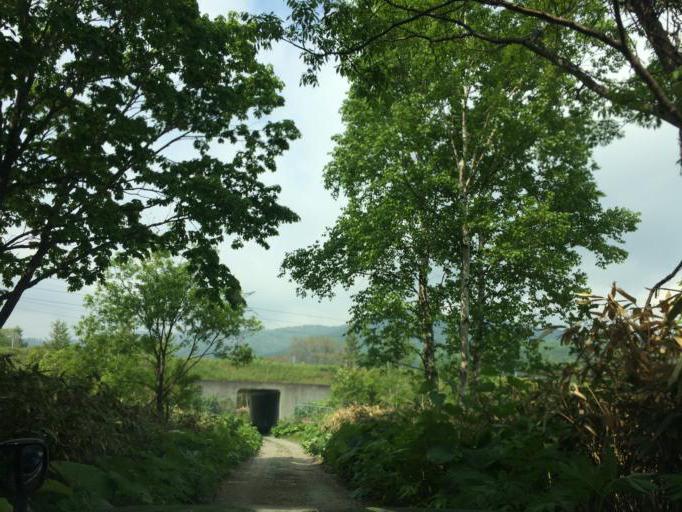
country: JP
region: Hokkaido
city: Niseko Town
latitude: 42.6429
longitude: 140.5013
